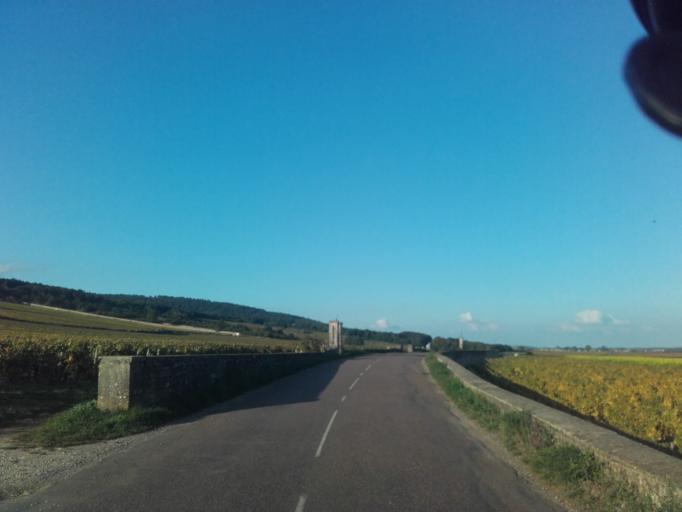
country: FR
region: Bourgogne
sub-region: Departement de la Cote-d'Or
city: Corpeau
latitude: 46.9443
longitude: 4.7384
